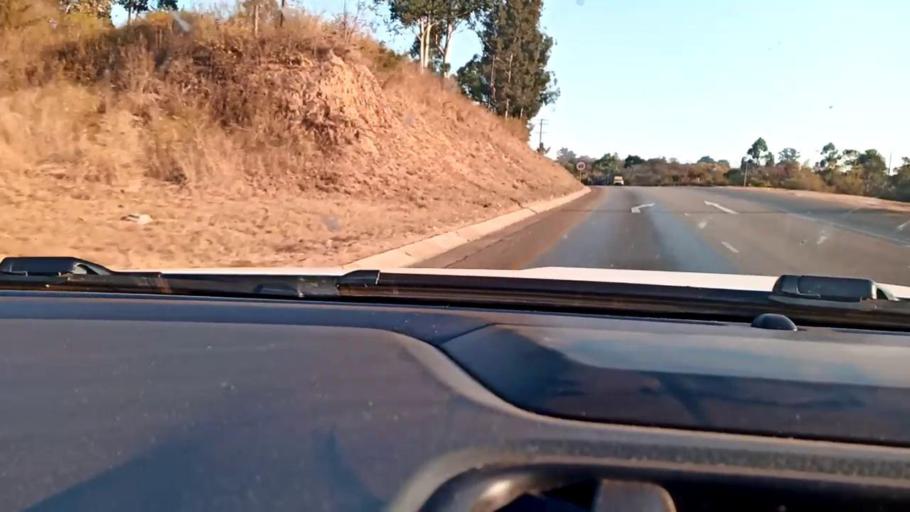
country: ZA
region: Limpopo
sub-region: Mopani District Municipality
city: Duiwelskloof
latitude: -23.6870
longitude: 30.1480
